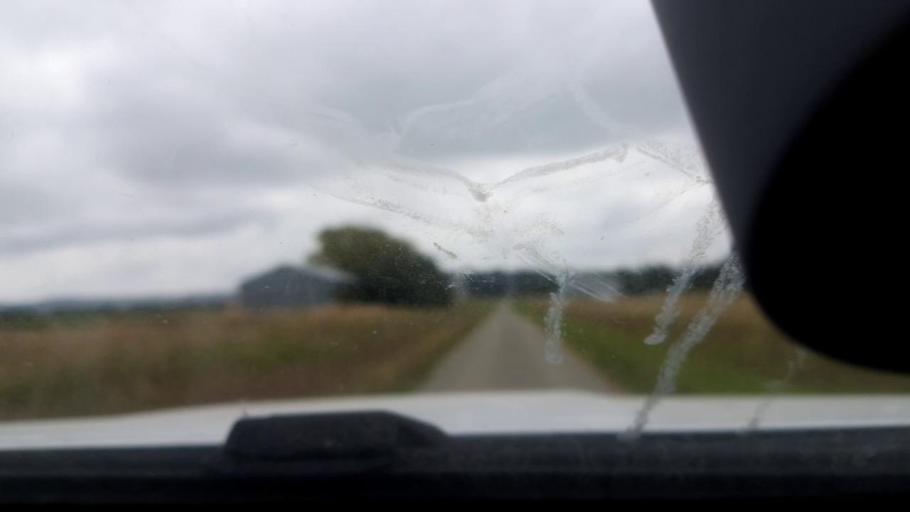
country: NZ
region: Canterbury
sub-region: Timaru District
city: Pleasant Point
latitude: -44.2266
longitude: 171.1649
